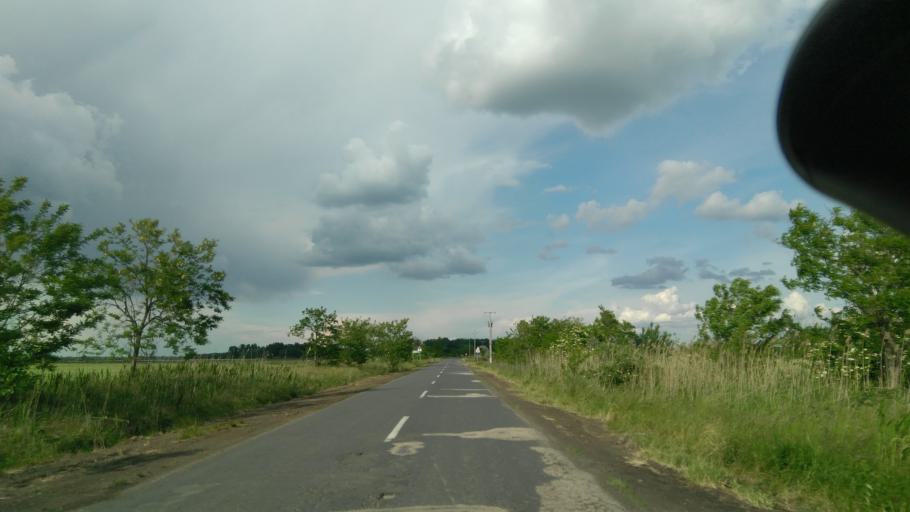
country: HU
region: Bekes
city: Dombegyhaz
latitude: 46.3269
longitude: 21.0946
